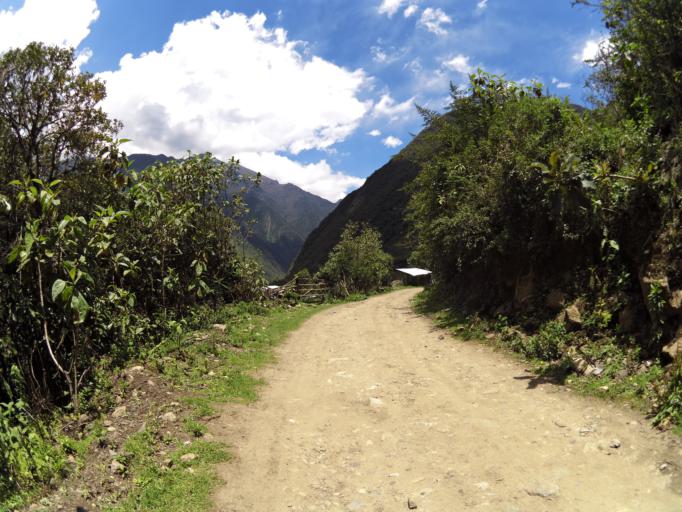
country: PE
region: Cusco
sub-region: Provincia de La Convencion
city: Santa Teresa
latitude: -13.3259
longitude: -72.6650
